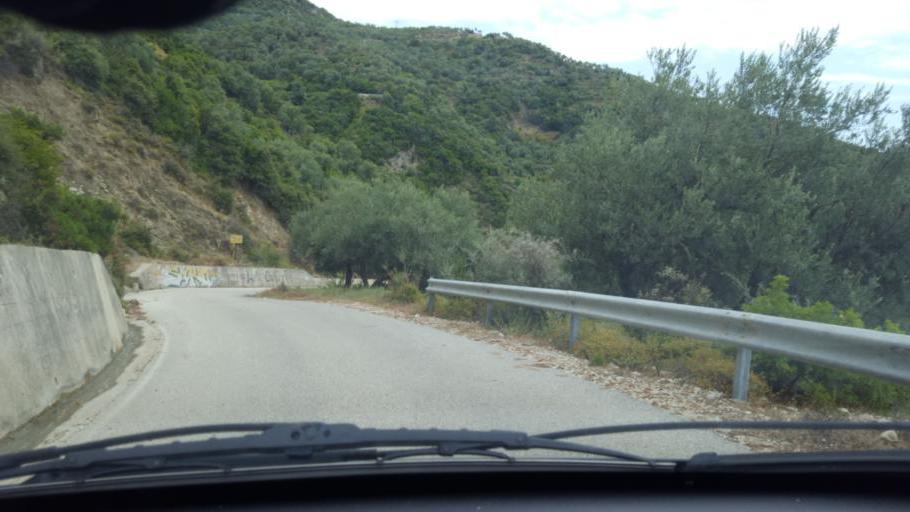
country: AL
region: Vlore
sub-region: Rrethi i Sarandes
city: Lukove
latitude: 39.9868
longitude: 19.9153
